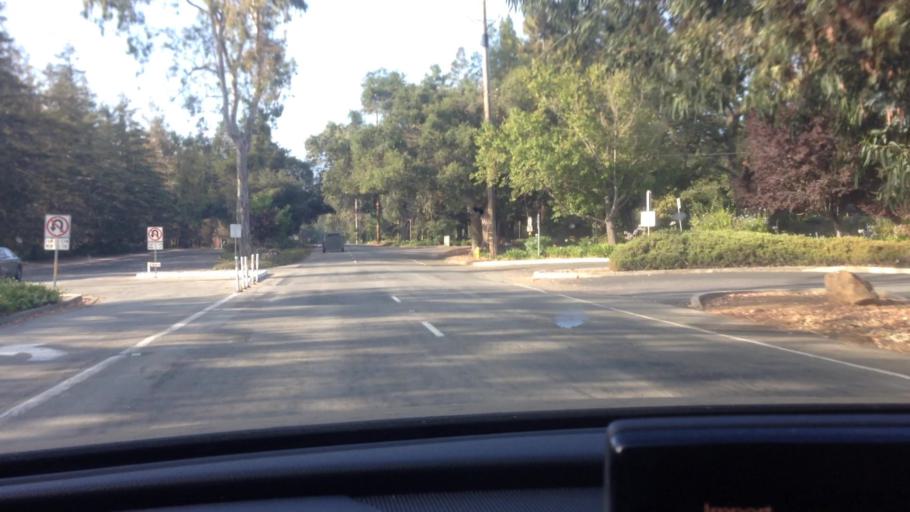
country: US
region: California
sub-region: Santa Clara County
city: Saratoga
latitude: 37.2656
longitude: -122.0139
